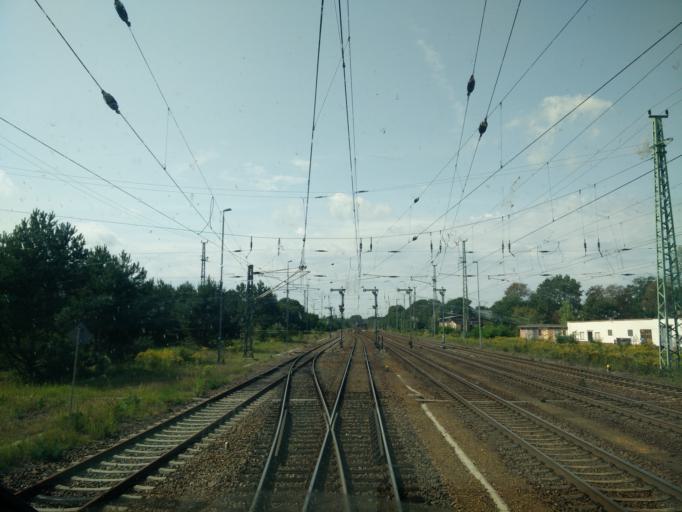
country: DE
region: Brandenburg
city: Calau
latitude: 51.7401
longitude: 13.9848
